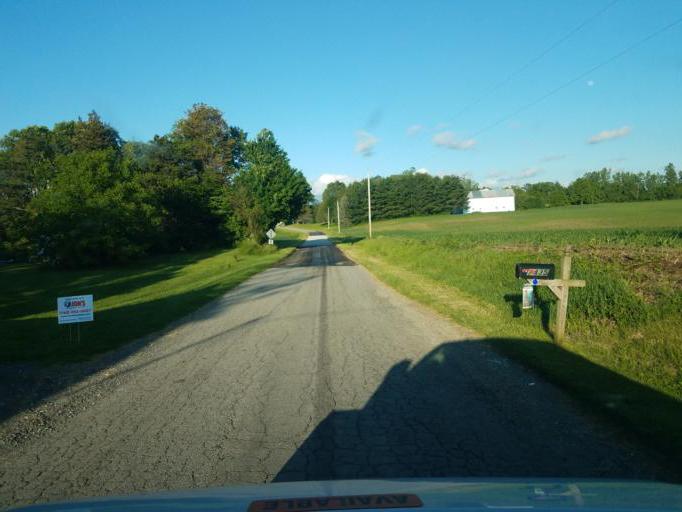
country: US
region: Ohio
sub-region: Knox County
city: Fredericktown
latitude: 40.4563
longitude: -82.6554
